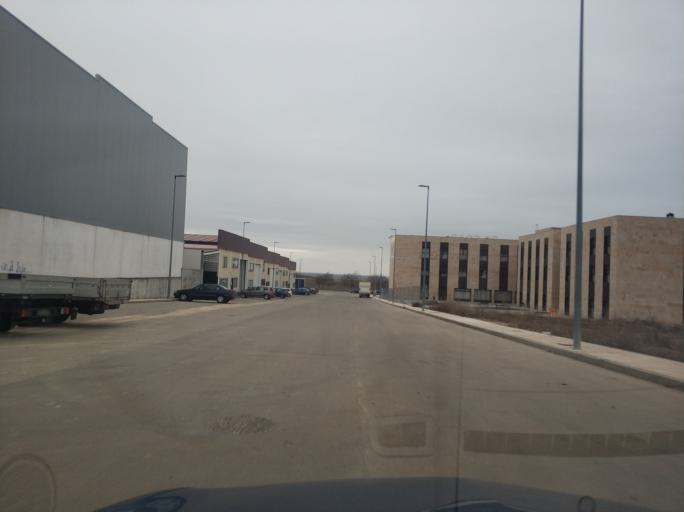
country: ES
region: Castille and Leon
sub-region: Provincia de Salamanca
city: Castellanos de Moriscos
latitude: 41.0101
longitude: -5.6067
